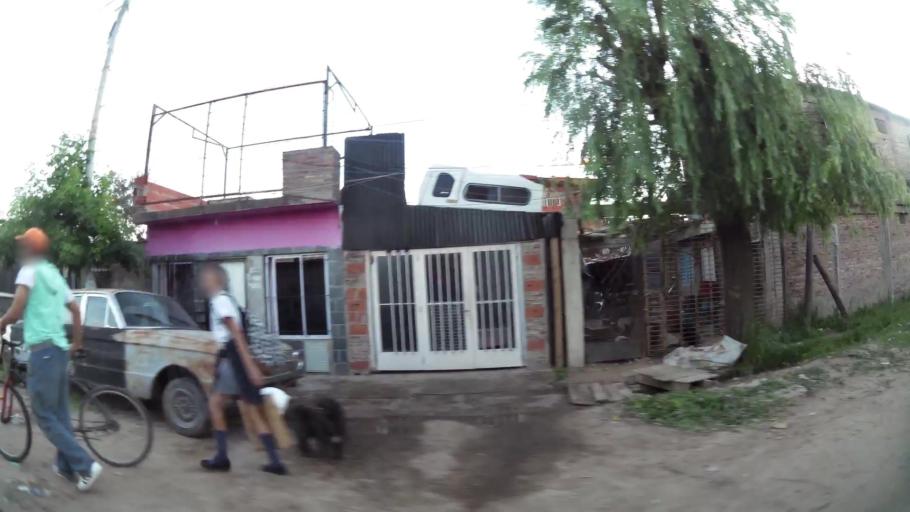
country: AR
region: Santa Fe
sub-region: Departamento de Rosario
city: Rosario
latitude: -32.9732
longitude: -60.6891
